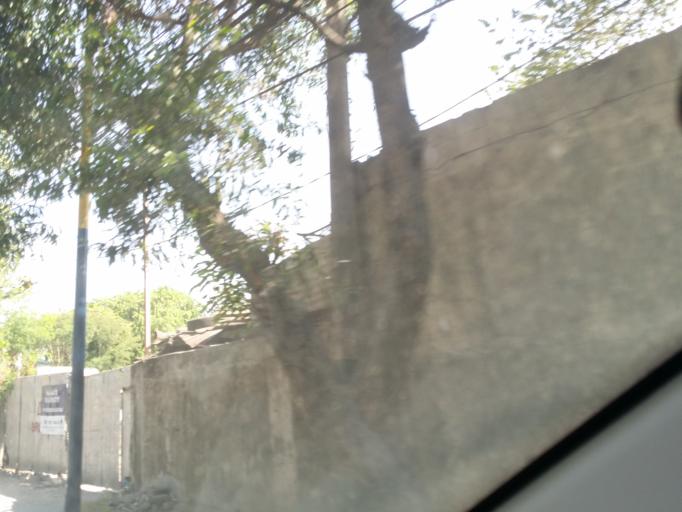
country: PH
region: Metro Manila
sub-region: Mandaluyong
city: Mandaluyong City
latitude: 14.5771
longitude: 121.0230
